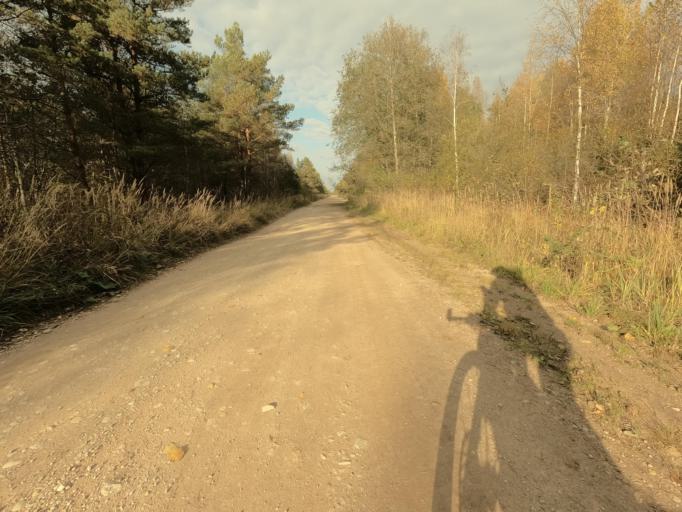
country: RU
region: Novgorod
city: Volkhovskiy
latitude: 58.8987
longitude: 31.0318
